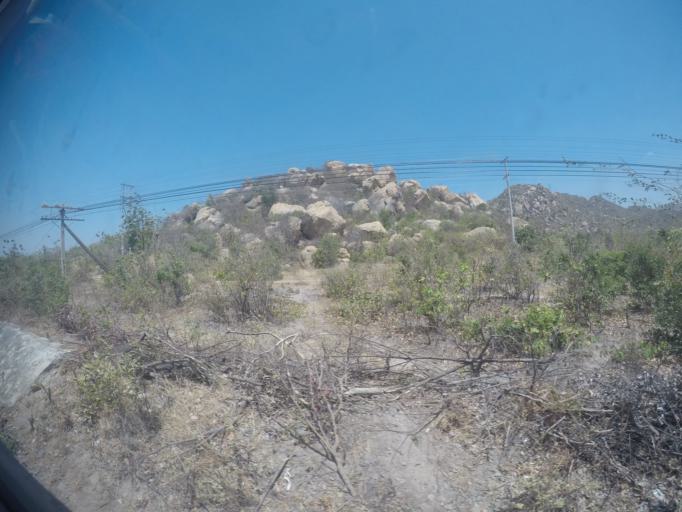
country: VN
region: Binh Thuan
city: Lien Huong
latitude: 11.3237
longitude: 108.8278
